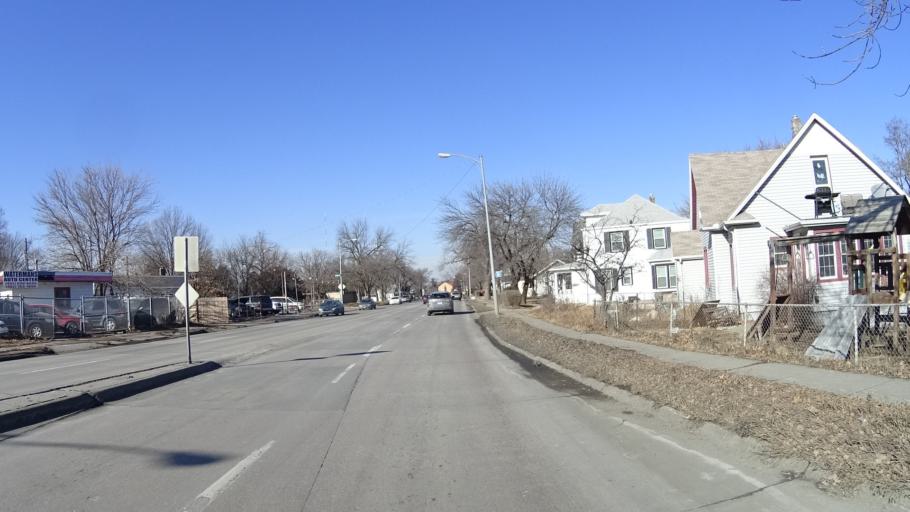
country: US
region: Nebraska
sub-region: Douglas County
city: Omaha
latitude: 41.2879
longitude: -96.0098
